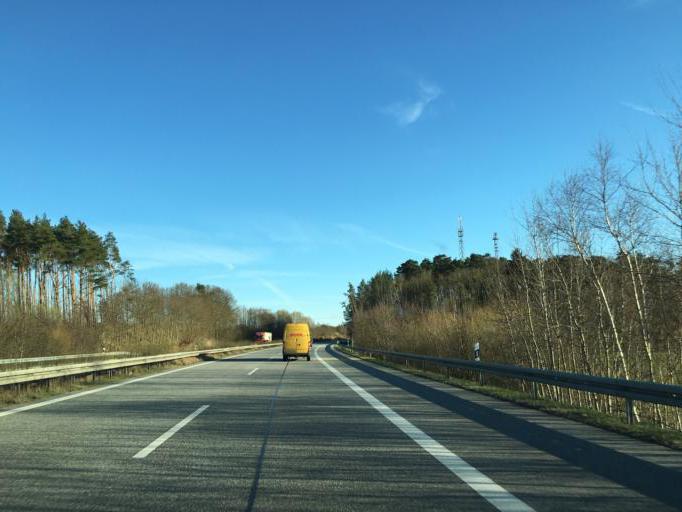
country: DE
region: Mecklenburg-Vorpommern
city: Lalendorf
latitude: 53.7269
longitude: 12.3539
